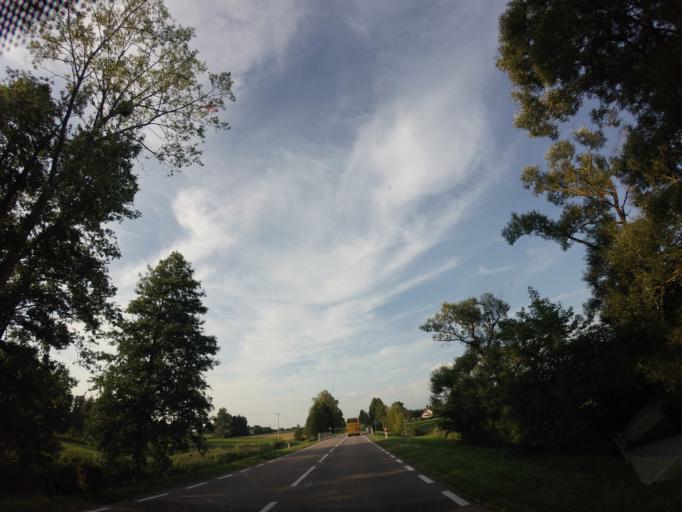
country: PL
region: Podlasie
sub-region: Powiat sejnenski
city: Sejny
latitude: 54.0676
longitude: 23.3622
